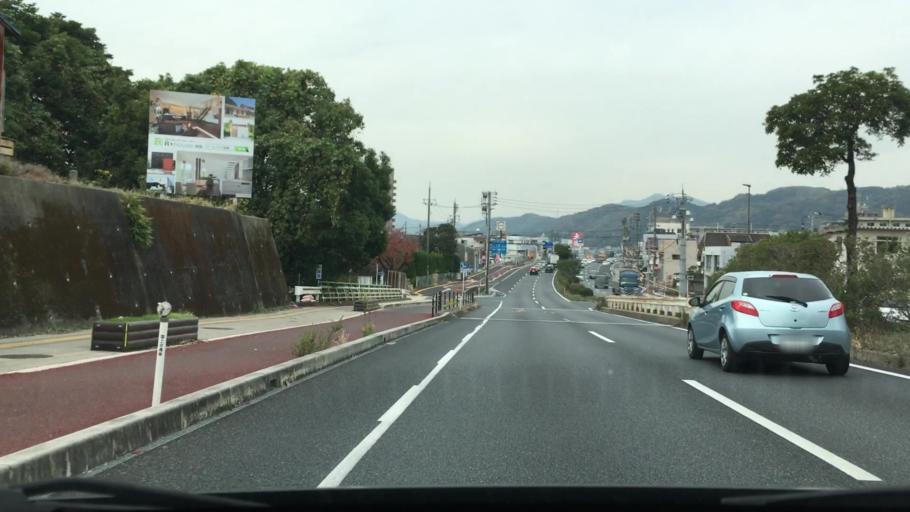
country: JP
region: Yamaguchi
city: Tokuyama
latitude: 34.0565
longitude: 131.8187
